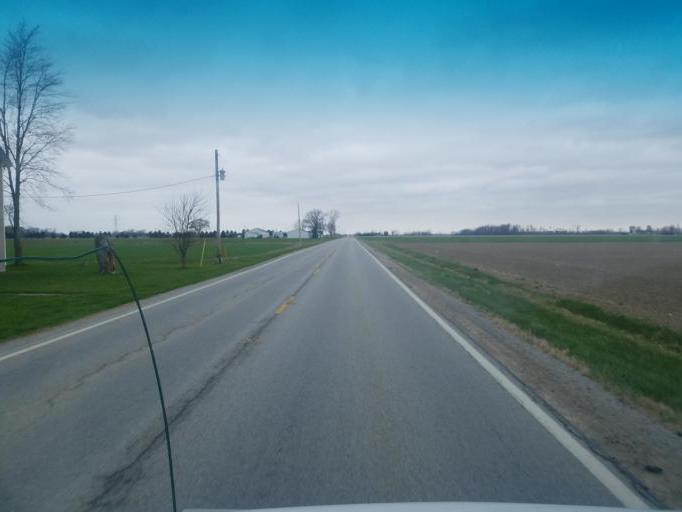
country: US
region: Ohio
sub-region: Allen County
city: Delphos
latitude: 40.9321
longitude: -84.4257
